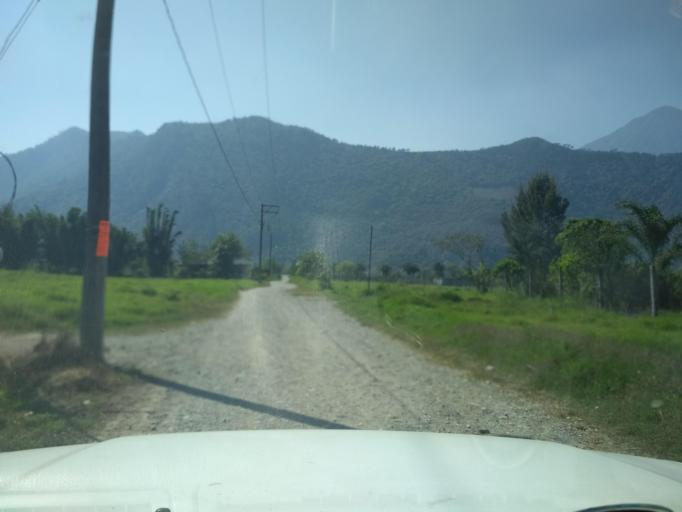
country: MX
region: Veracruz
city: Jalapilla
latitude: 18.8154
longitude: -97.0869
